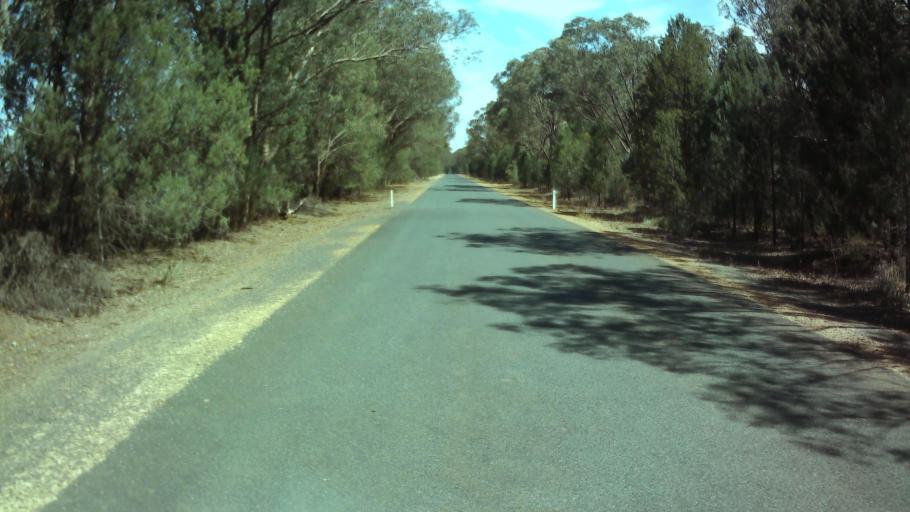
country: AU
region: New South Wales
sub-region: Weddin
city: Grenfell
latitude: -34.0170
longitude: 148.1293
